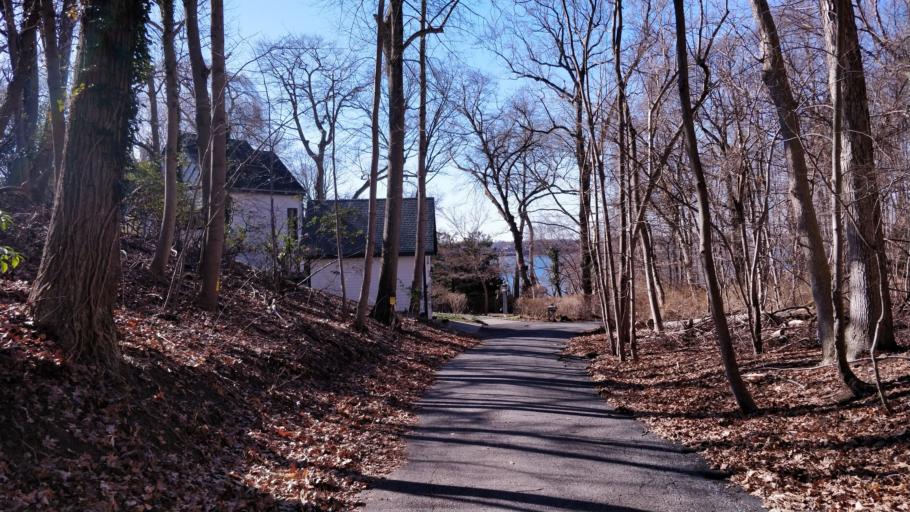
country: US
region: New York
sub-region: Suffolk County
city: Port Jefferson
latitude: 40.9615
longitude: -73.0727
